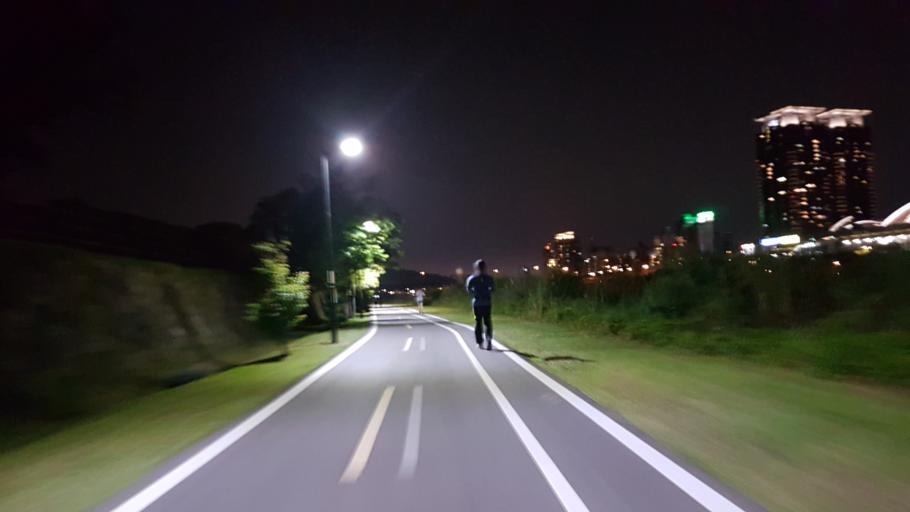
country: TW
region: Taipei
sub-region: Taipei
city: Banqiao
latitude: 24.9669
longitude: 121.5315
